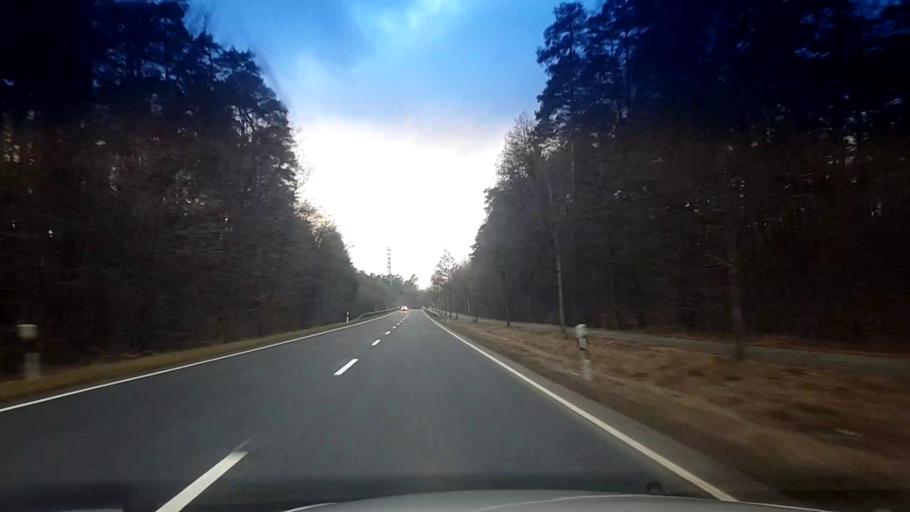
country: DE
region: Bavaria
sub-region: Upper Franconia
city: Memmelsdorf
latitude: 49.8892
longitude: 10.9541
